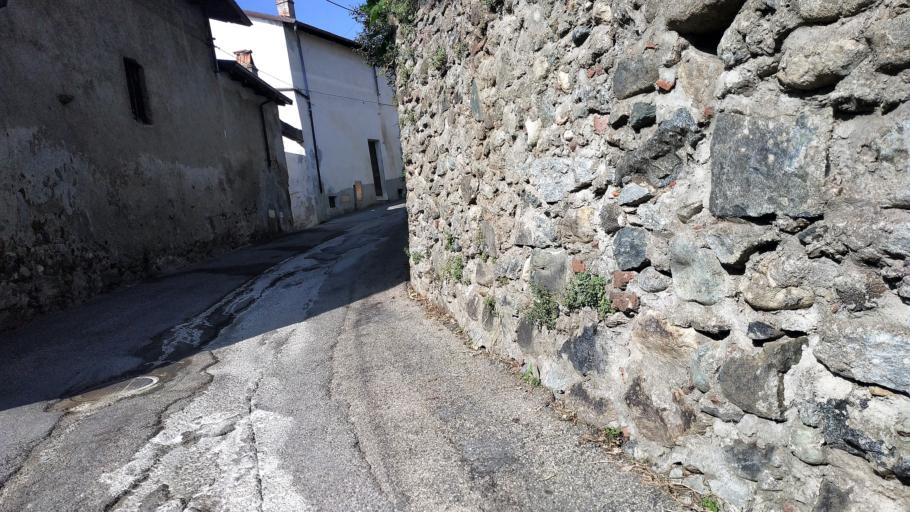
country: IT
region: Piedmont
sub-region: Provincia di Torino
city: Orio Canavese
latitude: 45.3305
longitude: 7.8607
